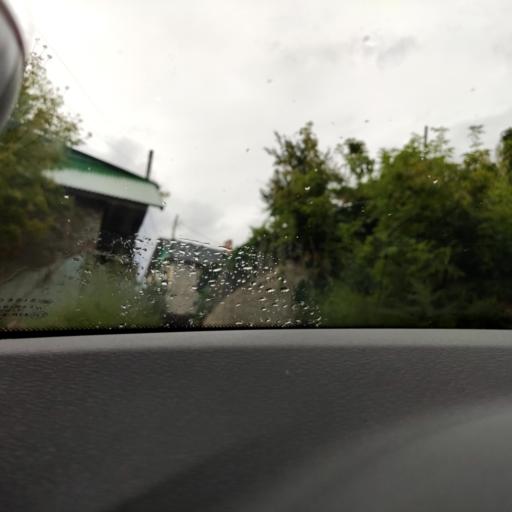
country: RU
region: Samara
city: Samara
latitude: 53.1727
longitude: 50.1578
